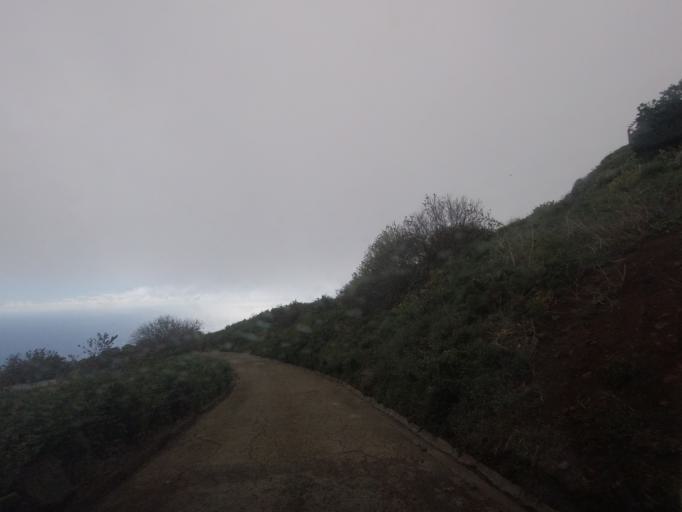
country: PT
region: Madeira
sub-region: Calheta
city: Faja da Ovelha
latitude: 32.7590
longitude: -17.2227
